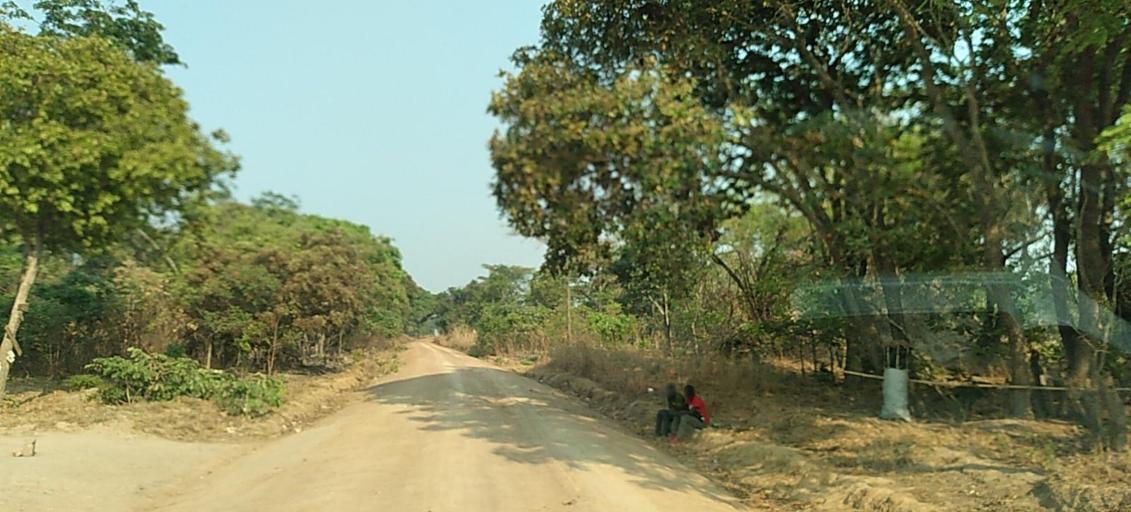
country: ZM
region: Copperbelt
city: Chingola
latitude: -12.8621
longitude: 27.5768
